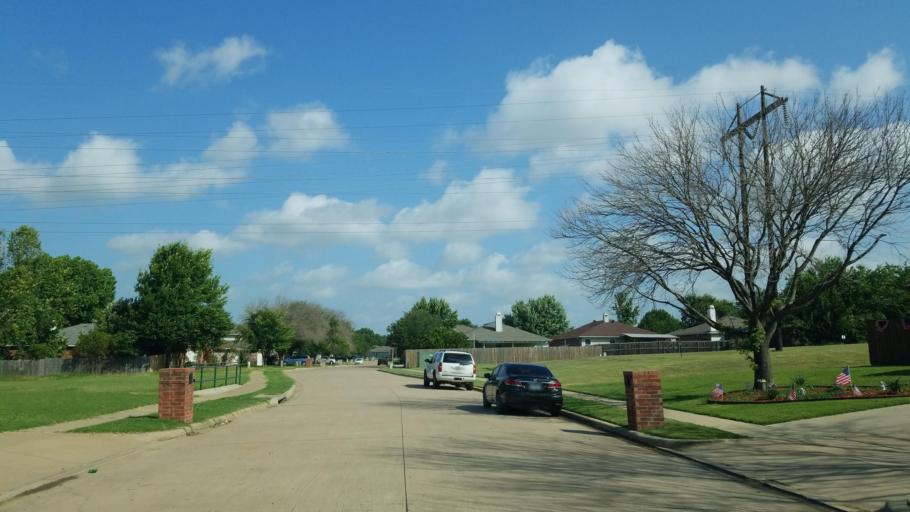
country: US
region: Texas
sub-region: Denton County
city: Copper Canyon
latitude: 33.1378
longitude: -97.1163
